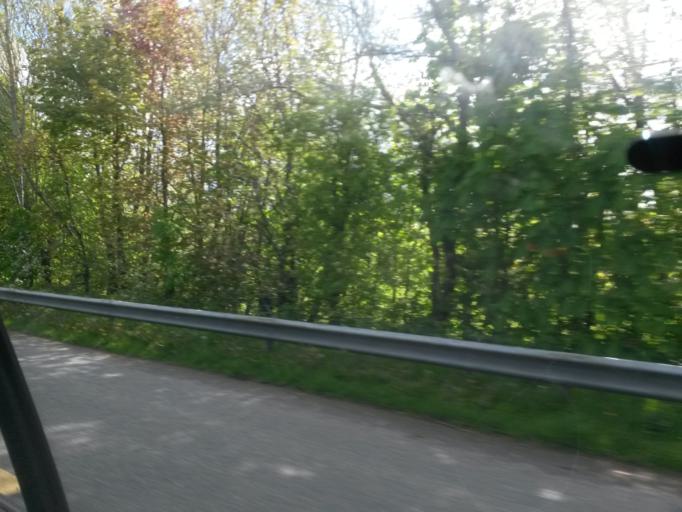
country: IE
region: Leinster
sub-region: Loch Garman
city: Enniscorthy
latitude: 52.5241
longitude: -6.5617
